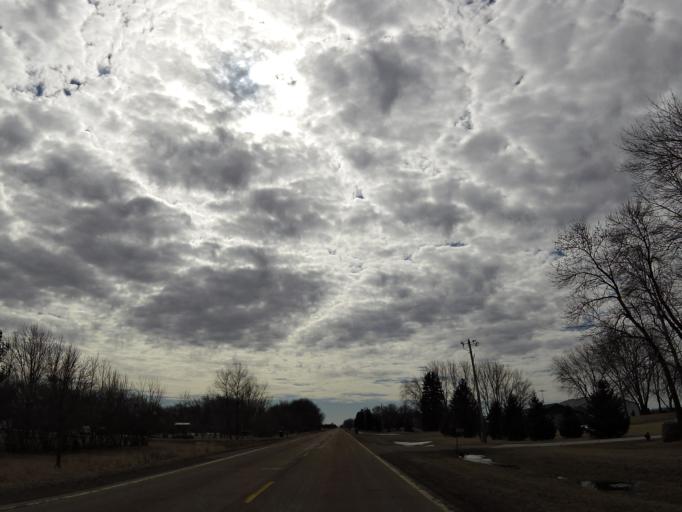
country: US
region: Minnesota
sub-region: Scott County
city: Prior Lake
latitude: 44.6597
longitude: -93.5165
